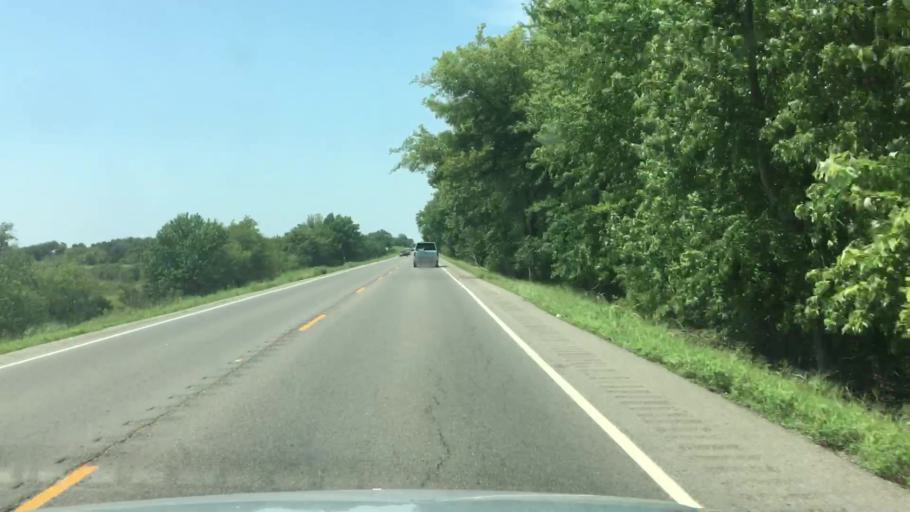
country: US
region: Oklahoma
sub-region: Wagoner County
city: Wagoner
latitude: 35.9371
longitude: -95.3319
